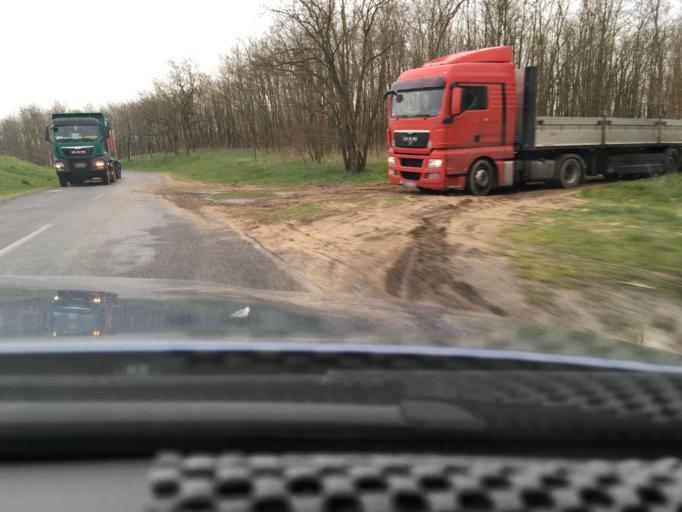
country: HU
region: Szabolcs-Szatmar-Bereg
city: Nyirbeltek
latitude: 47.6904
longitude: 22.0940
